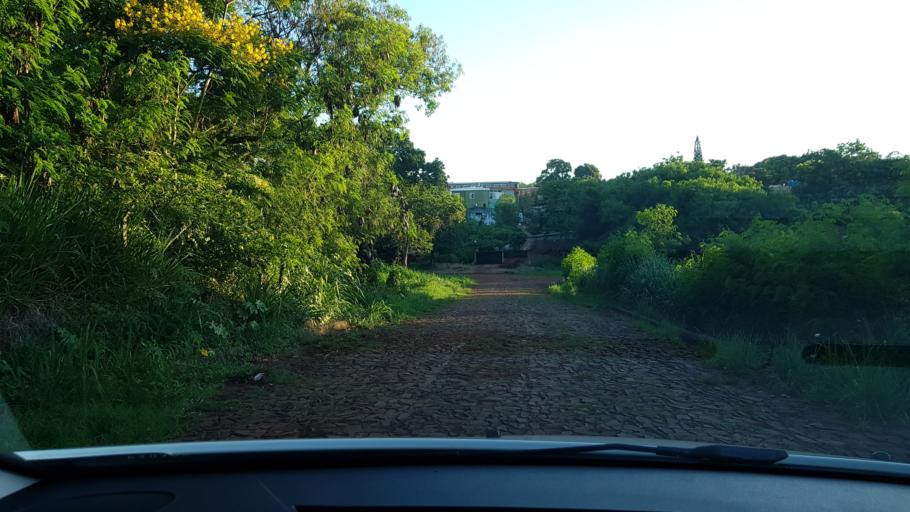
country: AR
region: Misiones
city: Puerto Libertad
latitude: -25.9195
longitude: -54.5809
